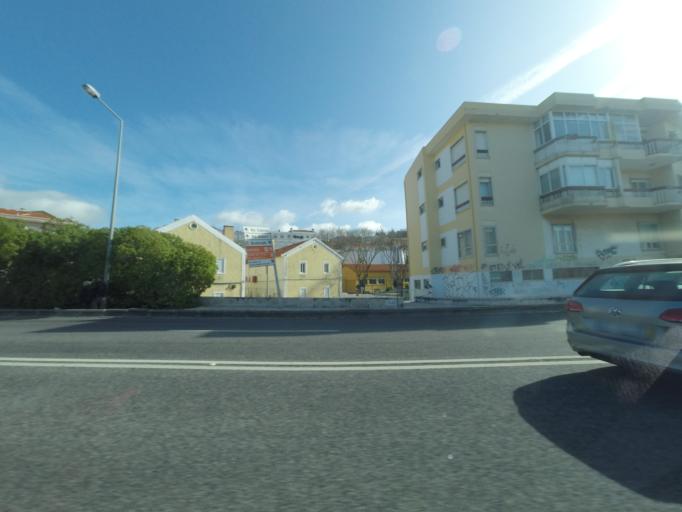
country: PT
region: Lisbon
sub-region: Oeiras
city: Linda-a-Velha
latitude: 38.7000
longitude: -9.2501
